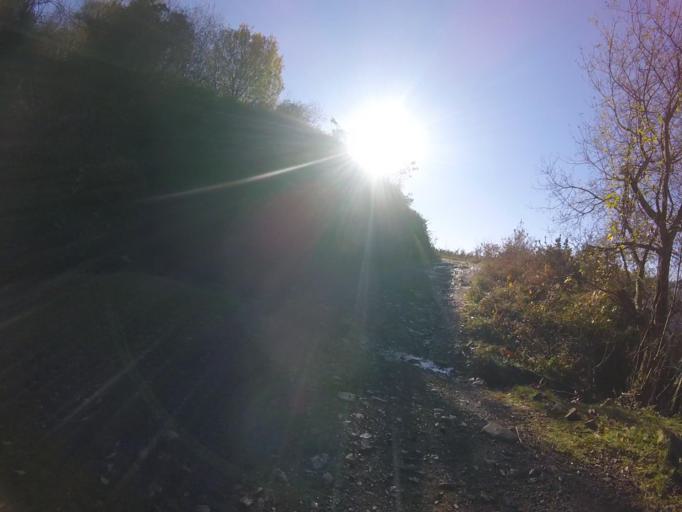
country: FR
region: Aquitaine
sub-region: Departement des Pyrenees-Atlantiques
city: Urrugne
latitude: 43.3272
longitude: -1.7301
